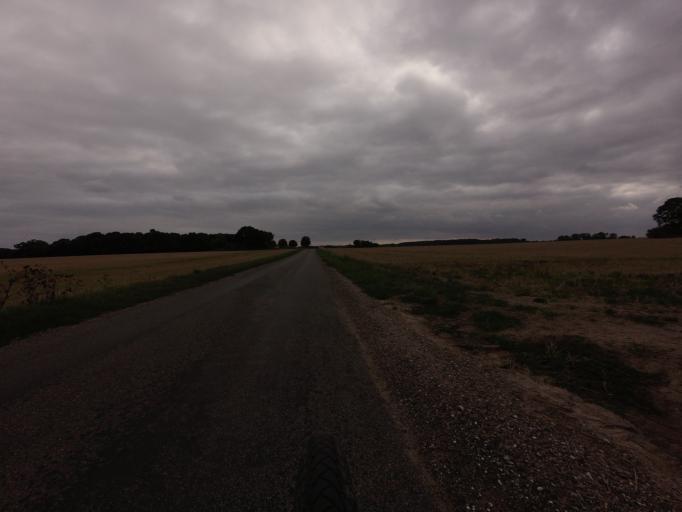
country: DK
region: Zealand
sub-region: Stevns Kommune
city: Store Heddinge
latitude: 55.3330
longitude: 12.3308
